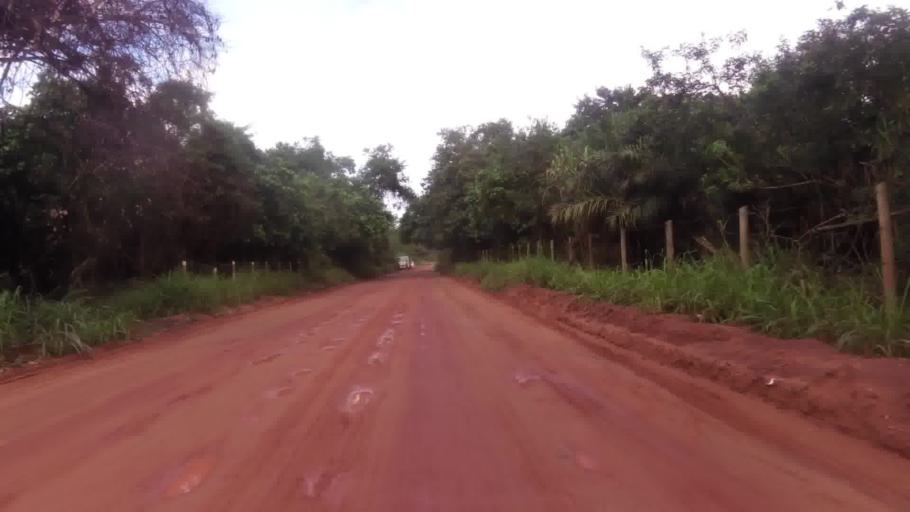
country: BR
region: Espirito Santo
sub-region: Piuma
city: Piuma
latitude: -20.7920
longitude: -40.6343
